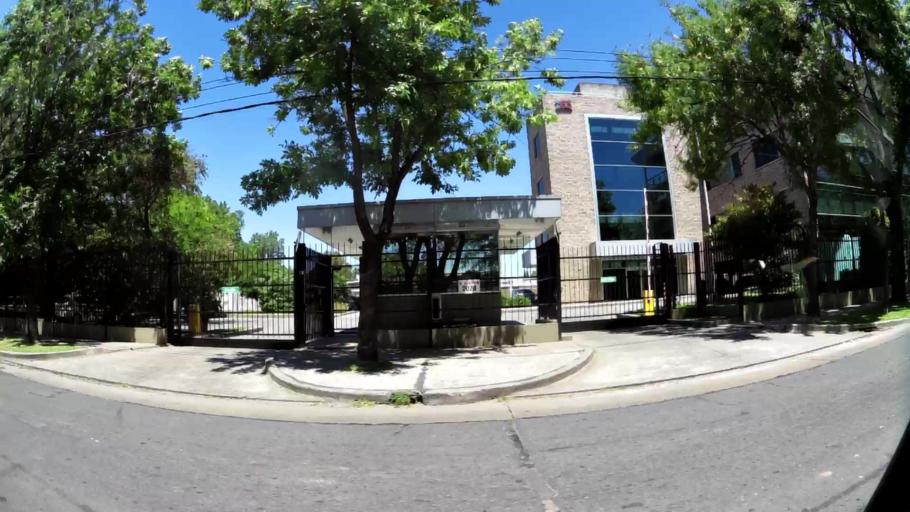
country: AR
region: Buenos Aires
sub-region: Partido de San Isidro
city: San Isidro
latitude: -34.5003
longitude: -58.5238
